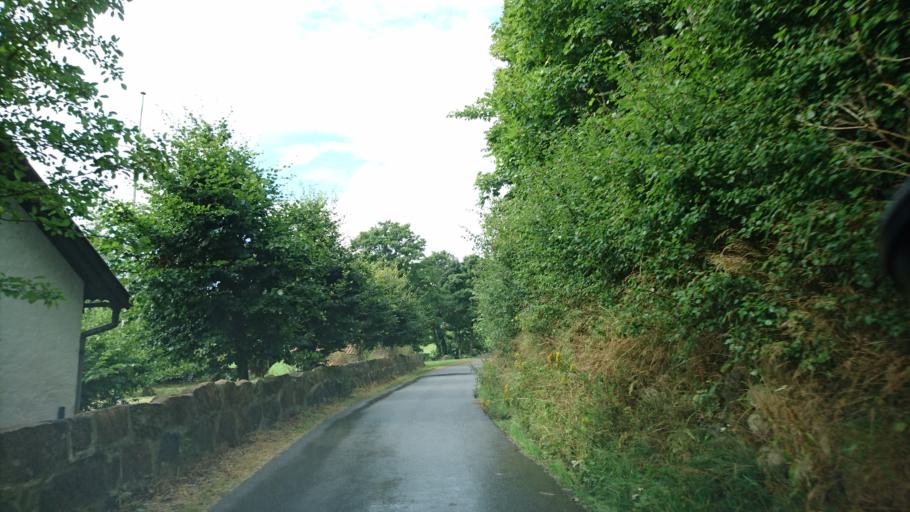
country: DK
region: North Denmark
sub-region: Frederikshavn Kommune
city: Frederikshavn
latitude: 57.4011
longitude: 10.4754
